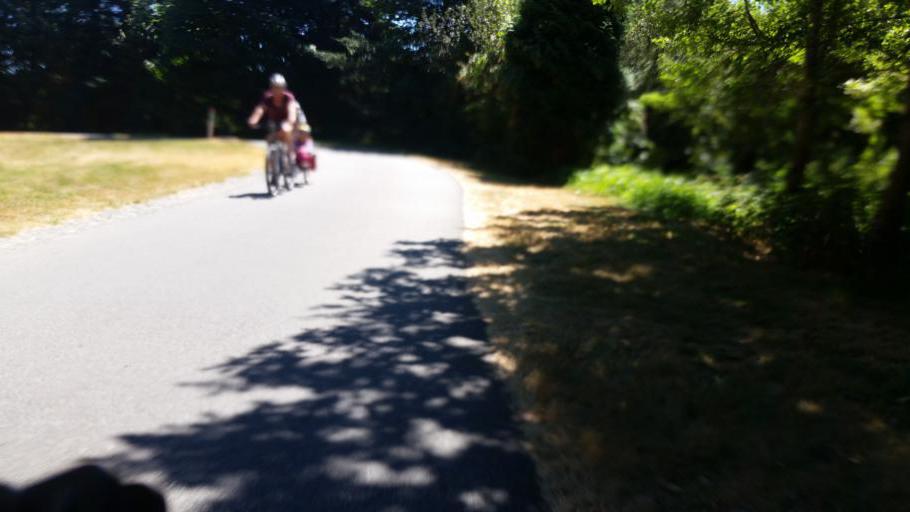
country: US
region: Washington
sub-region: King County
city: Woodinville
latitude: 47.7495
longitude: -122.1644
